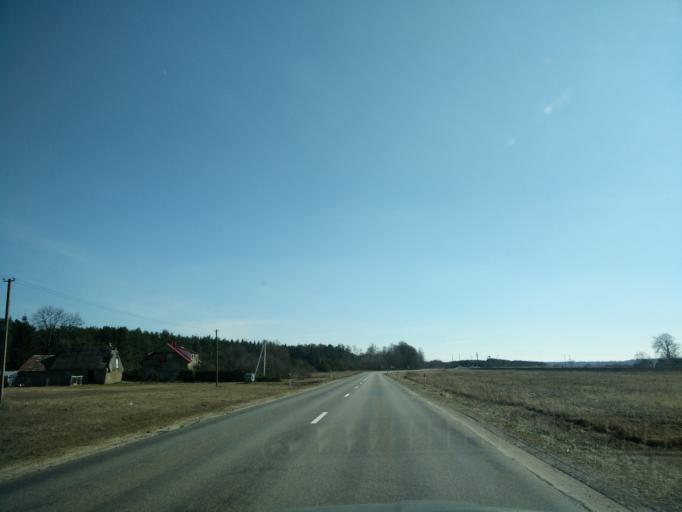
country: LT
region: Klaipedos apskritis
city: Silute
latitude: 55.3293
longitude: 21.5198
